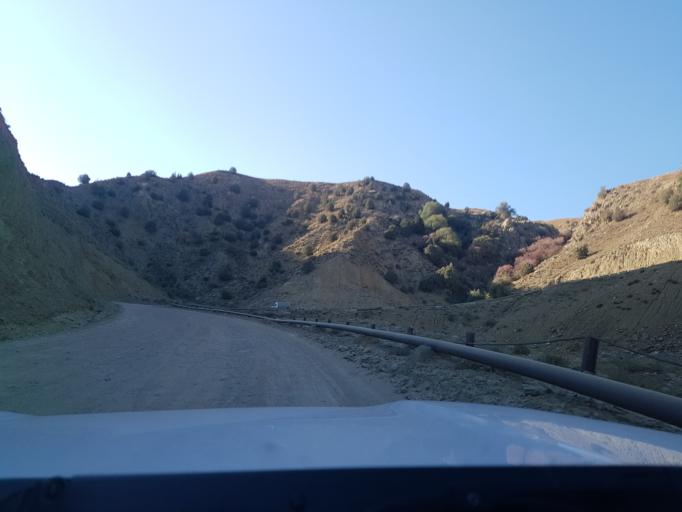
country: TM
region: Ahal
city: Baharly
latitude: 38.4428
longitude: 57.0476
